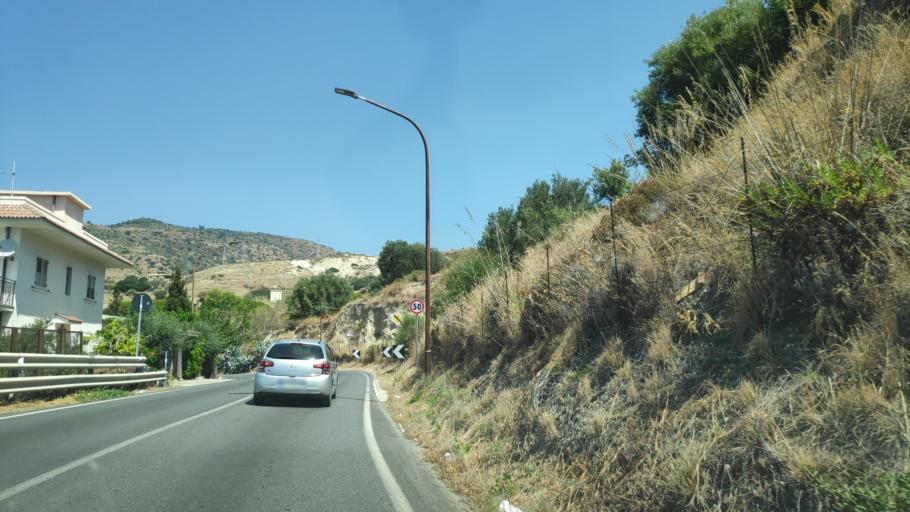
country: IT
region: Calabria
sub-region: Provincia di Reggio Calabria
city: Palizzi Marina
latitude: 37.9167
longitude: 15.9975
